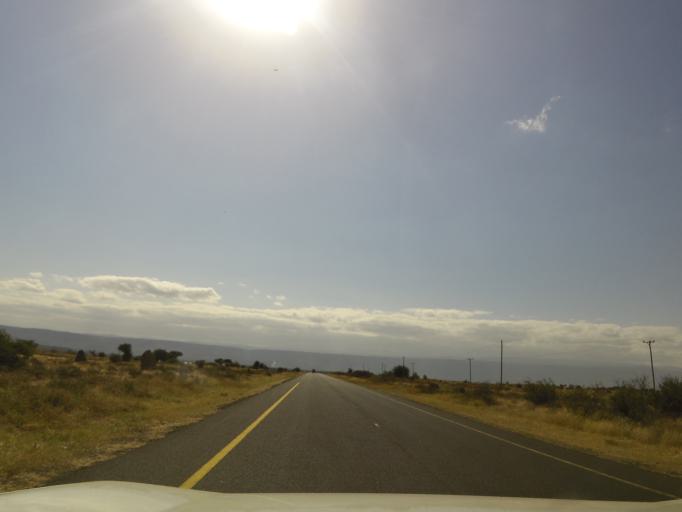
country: TZ
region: Arusha
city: Mto wa Mbu
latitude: -3.3989
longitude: 35.9084
